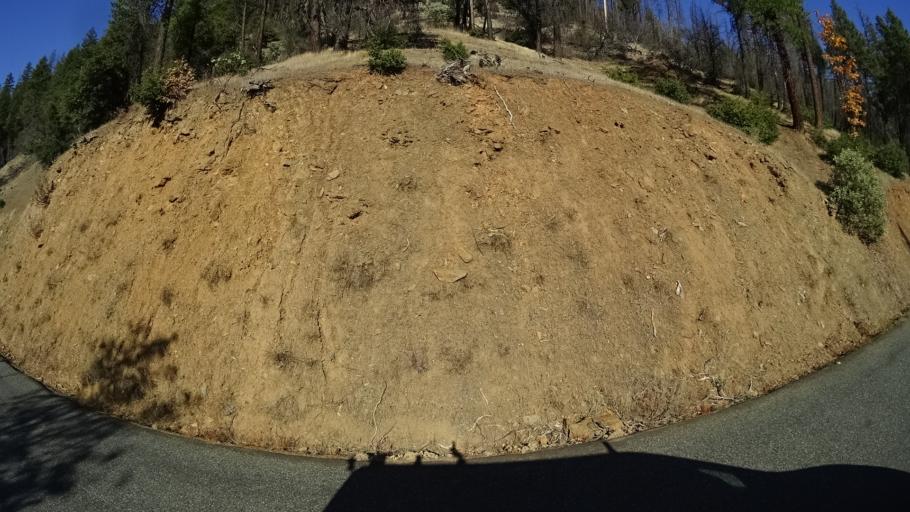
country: US
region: California
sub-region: Siskiyou County
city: Happy Camp
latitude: 41.7033
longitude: -123.0396
